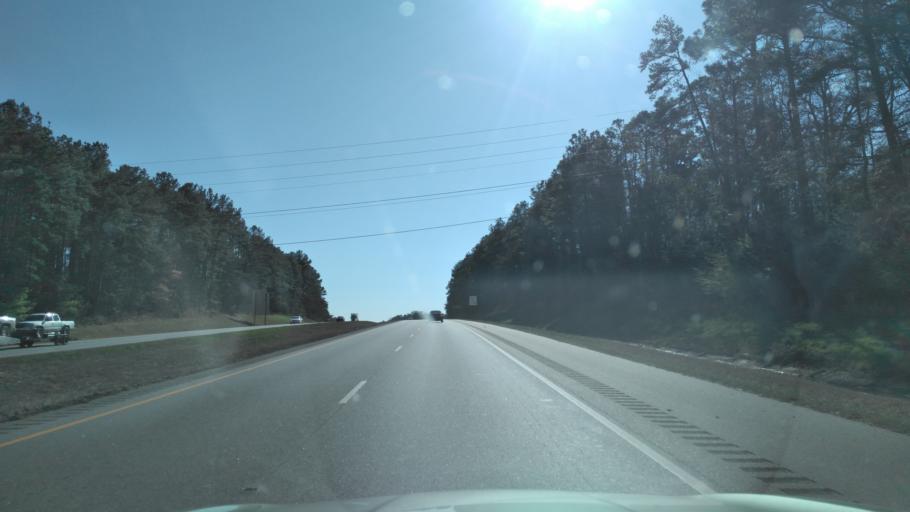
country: US
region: Alabama
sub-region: Butler County
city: Greenville
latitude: 31.8452
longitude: -86.6487
